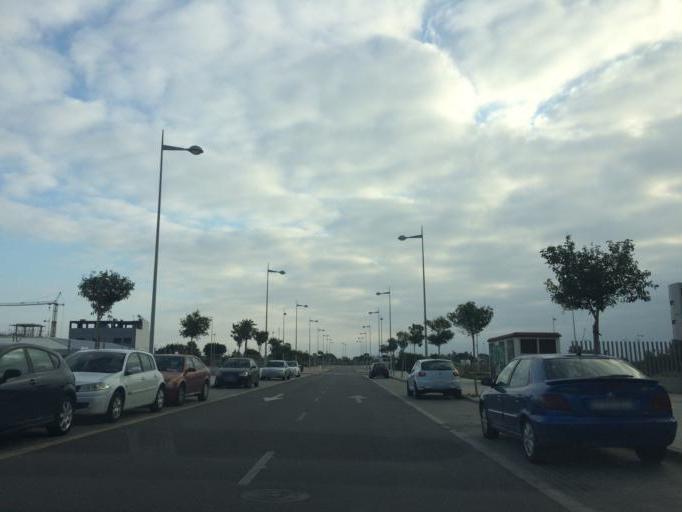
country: ES
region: Andalusia
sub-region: Provincia de Almeria
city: Almeria
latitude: 36.8284
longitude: -2.4407
